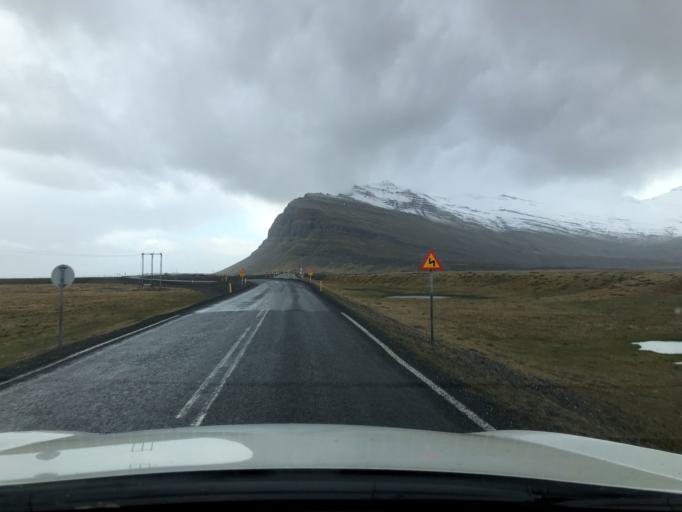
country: IS
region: East
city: Hoefn
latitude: 64.1607
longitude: -15.9309
